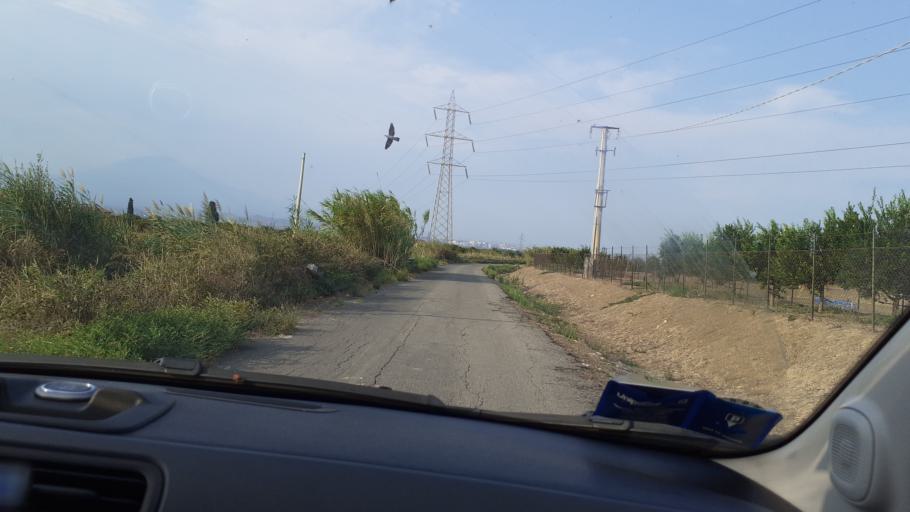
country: IT
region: Sicily
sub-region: Catania
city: Catania
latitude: 37.4241
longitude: 15.0093
